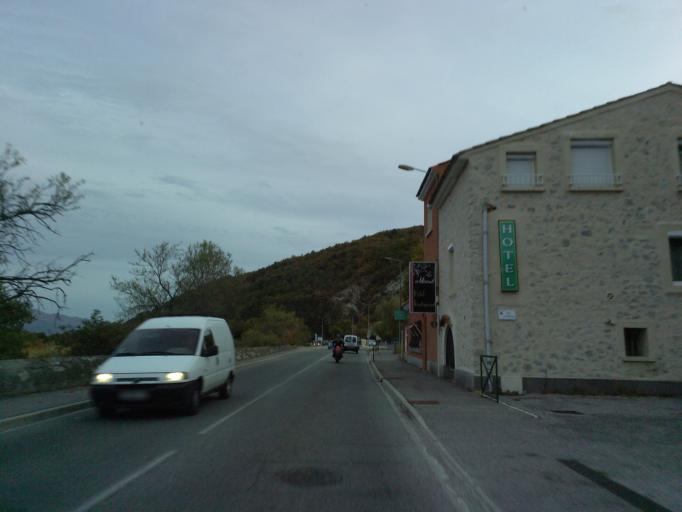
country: FR
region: Provence-Alpes-Cote d'Azur
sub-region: Departement des Alpes-de-Haute-Provence
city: Peipin
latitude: 44.1567
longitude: 5.9512
